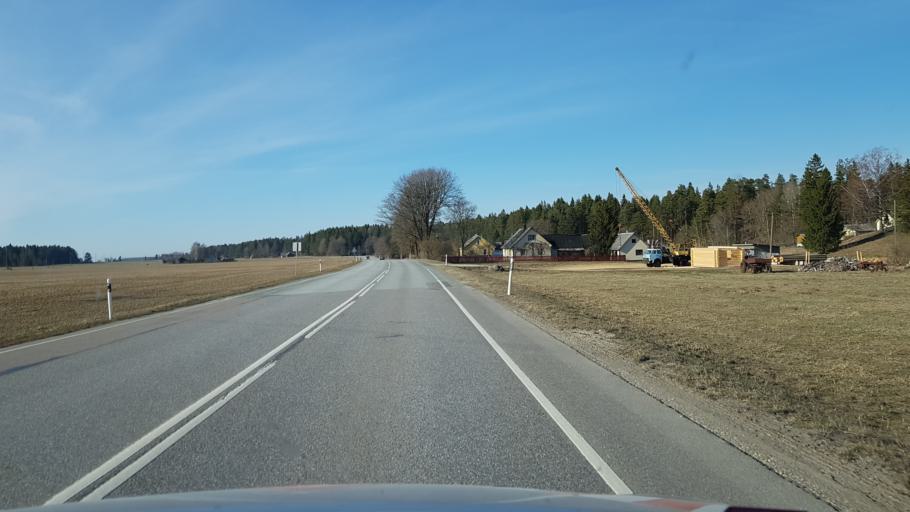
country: EE
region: Laeaene-Virumaa
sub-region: Vinni vald
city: Vinni
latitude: 59.1813
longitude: 26.5771
